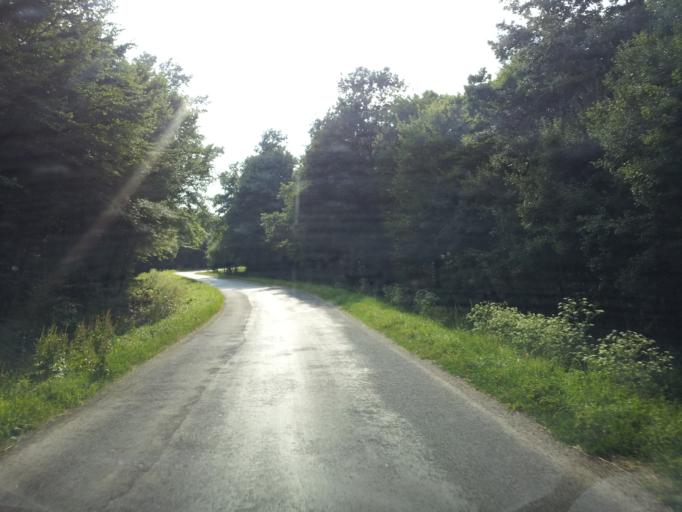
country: HU
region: Veszprem
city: Zanka
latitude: 46.9657
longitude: 17.6617
